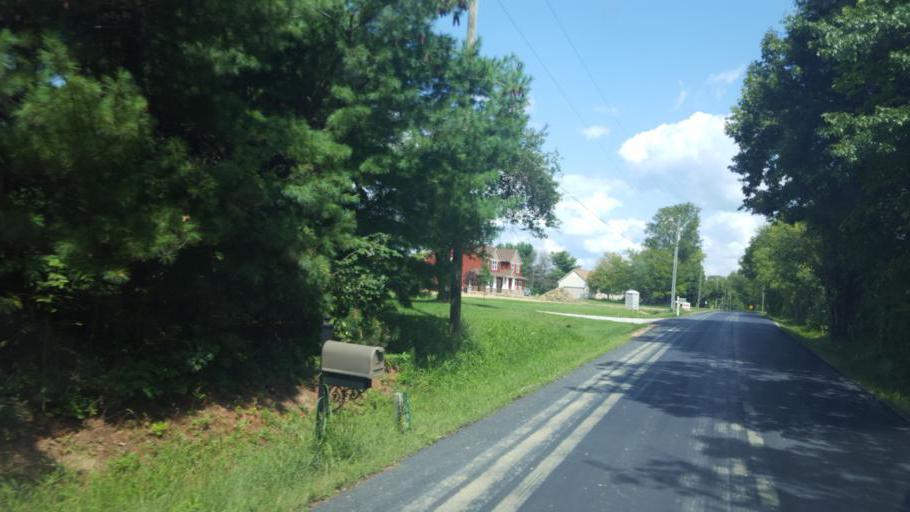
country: US
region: Ohio
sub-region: Delaware County
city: Lewis Center
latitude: 40.2534
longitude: -82.9443
